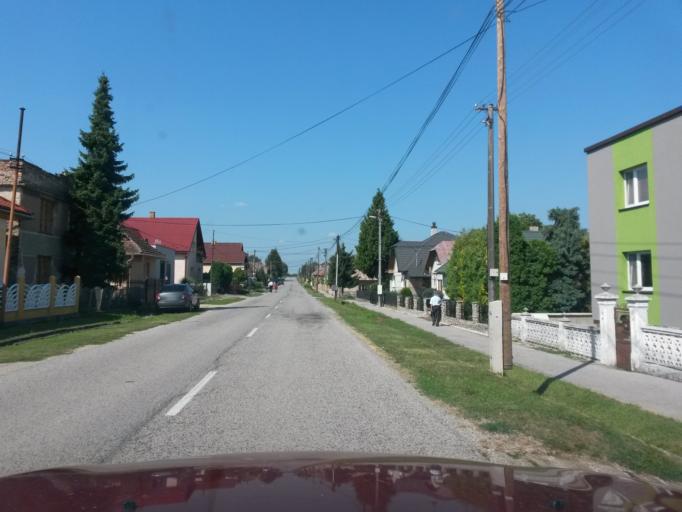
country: HU
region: Borsod-Abauj-Zemplen
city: Gonc
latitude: 48.5344
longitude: 21.1848
